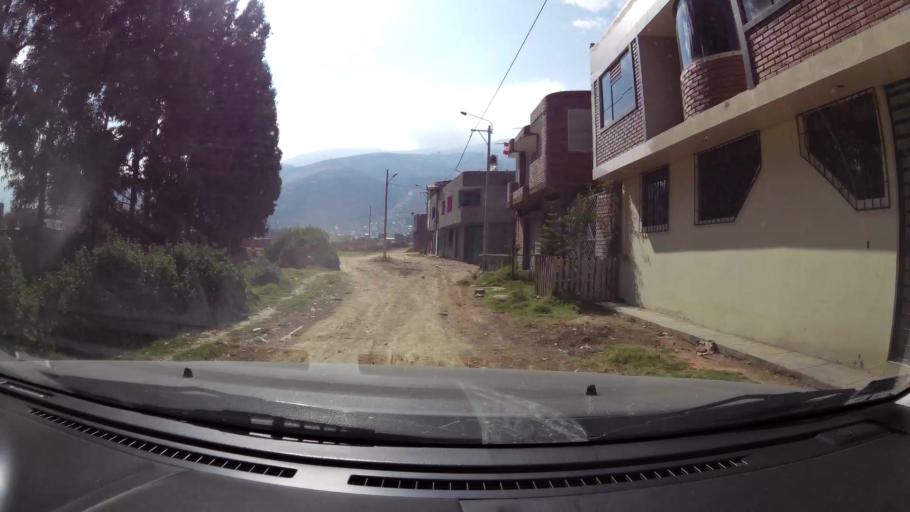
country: PE
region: Junin
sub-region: Provincia de Huancayo
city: Huancayo
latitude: -12.0554
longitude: -75.1941
